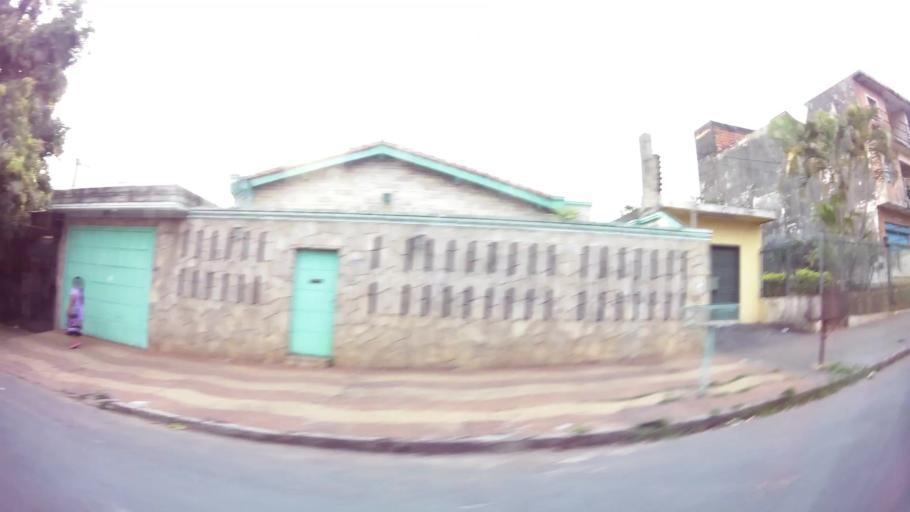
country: PY
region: Central
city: Lambare
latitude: -25.3240
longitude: -57.5744
